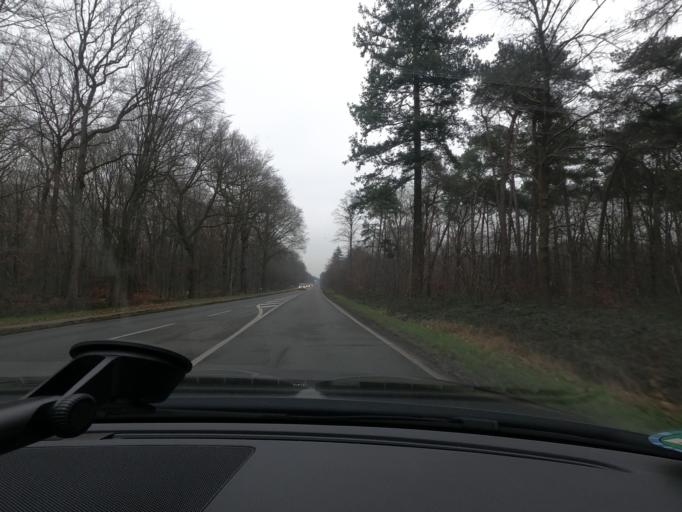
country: DE
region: North Rhine-Westphalia
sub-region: Regierungsbezirk Dusseldorf
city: Nettetal
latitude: 51.3557
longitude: 6.2381
